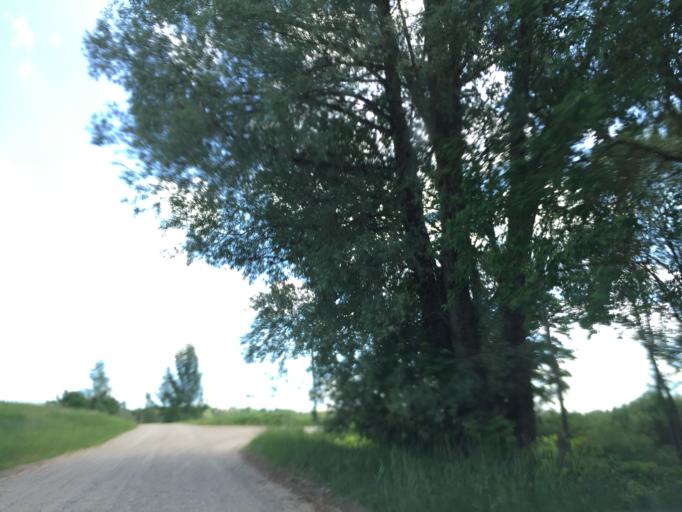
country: LV
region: Priekuli
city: Priekuli
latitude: 57.2549
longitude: 25.4308
